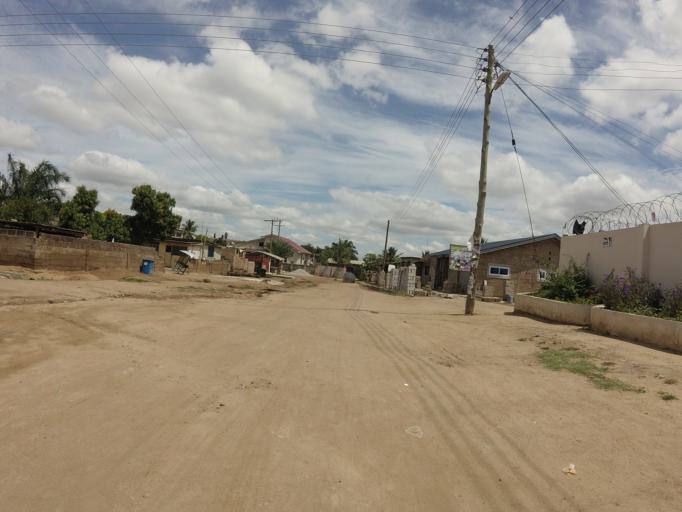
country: GH
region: Central
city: Kasoa
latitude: 5.5451
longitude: -0.4013
